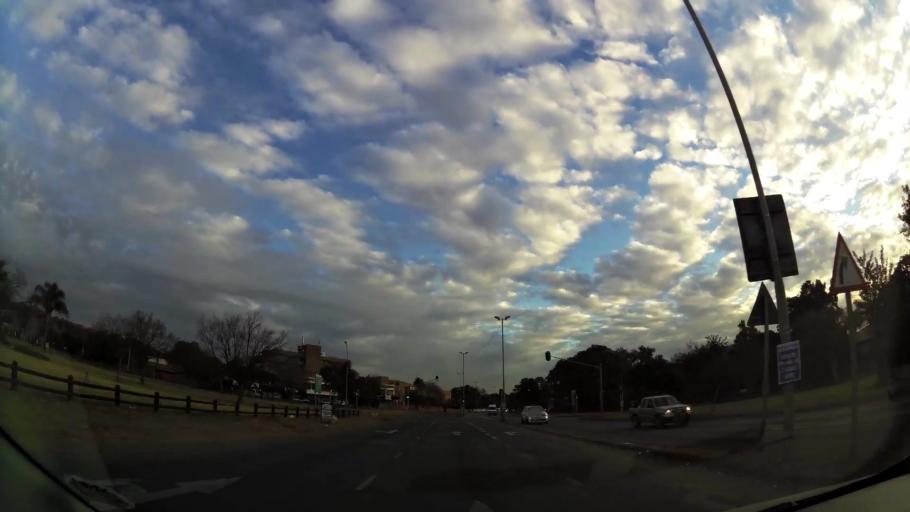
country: ZA
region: Gauteng
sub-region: City of Tshwane Metropolitan Municipality
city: Pretoria
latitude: -25.7391
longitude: 28.3107
